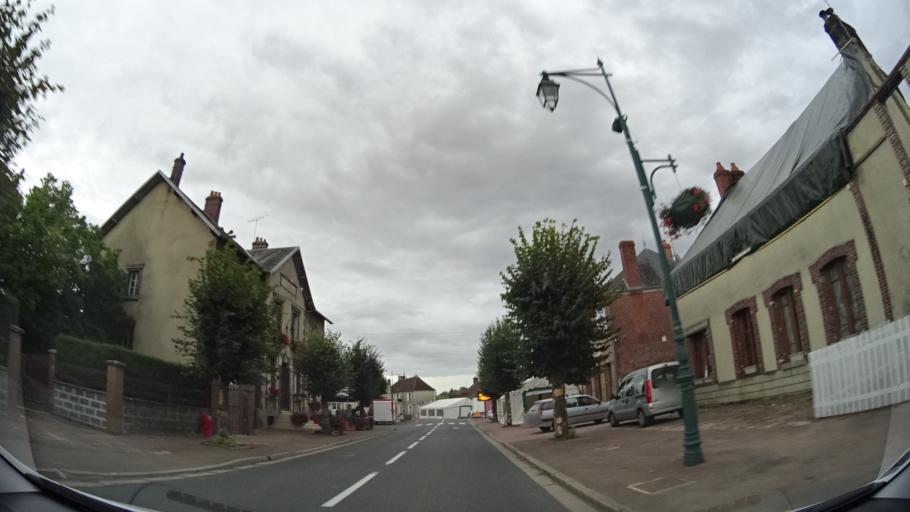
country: FR
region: Centre
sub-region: Departement du Loiret
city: Trigueres
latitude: 47.9393
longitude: 2.9844
